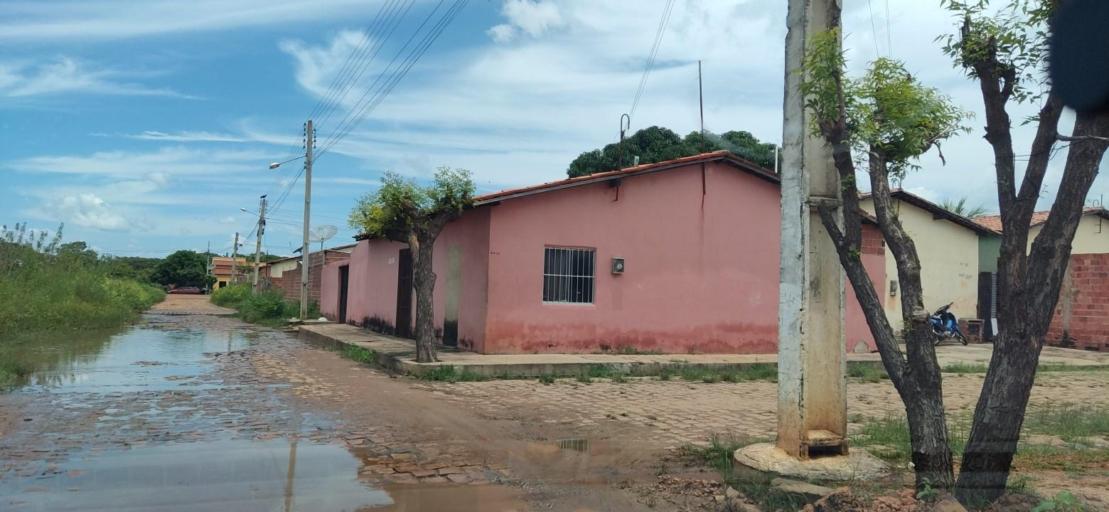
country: BR
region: Piaui
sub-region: Valenca Do Piaui
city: Valenca do Piaui
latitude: -6.4160
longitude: -41.7294
